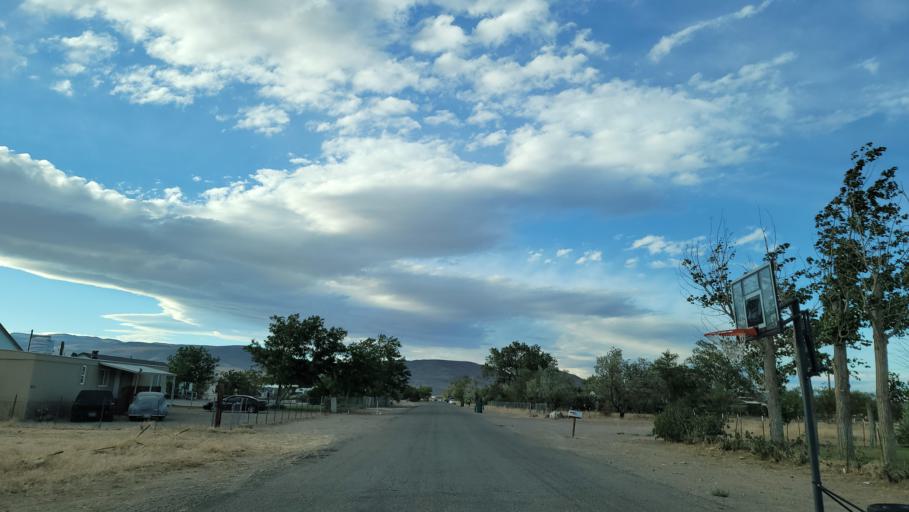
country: US
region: Nevada
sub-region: Lyon County
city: Silver Springs
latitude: 39.3922
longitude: -119.2373
